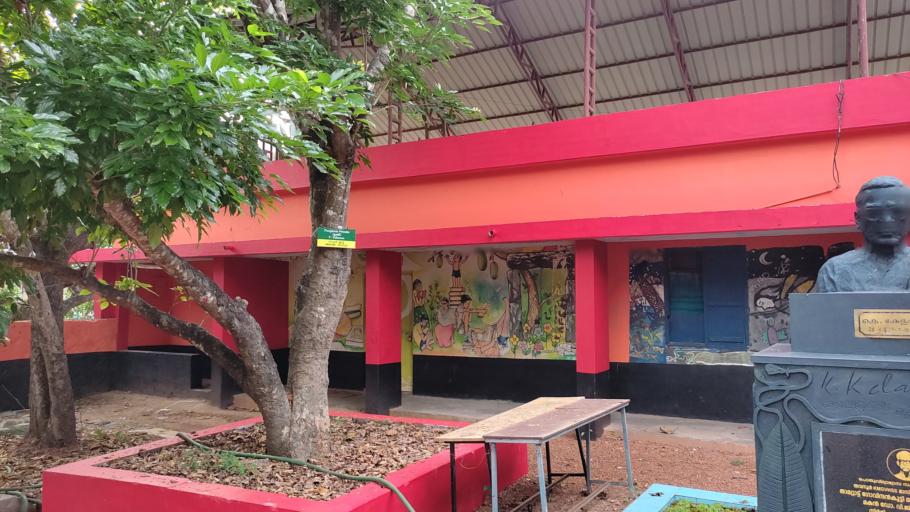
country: IN
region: Kerala
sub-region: Malappuram
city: Tirur
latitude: 10.8545
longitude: 75.9838
